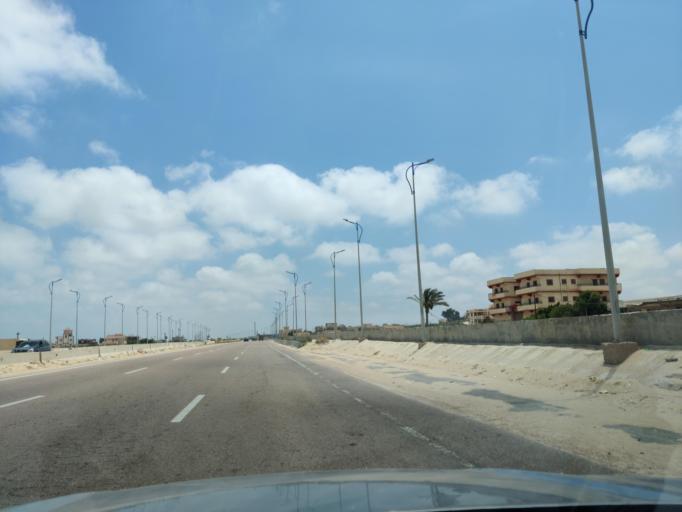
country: EG
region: Alexandria
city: Alexandria
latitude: 30.9611
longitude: 29.5443
